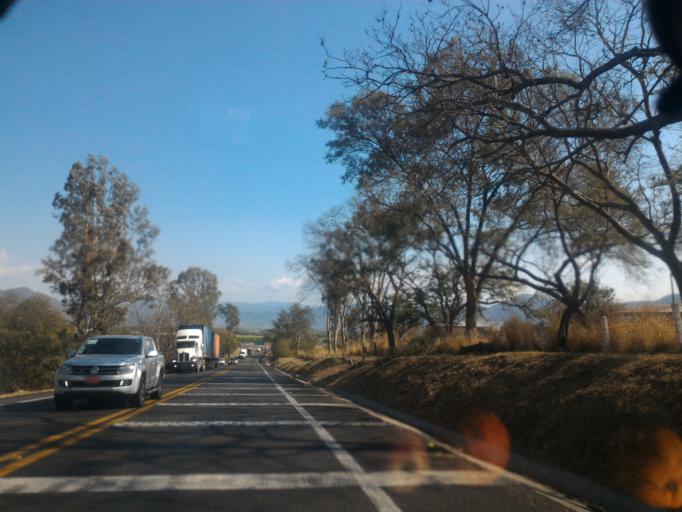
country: MX
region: Jalisco
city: Tuxpan
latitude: 19.5403
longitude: -103.4254
